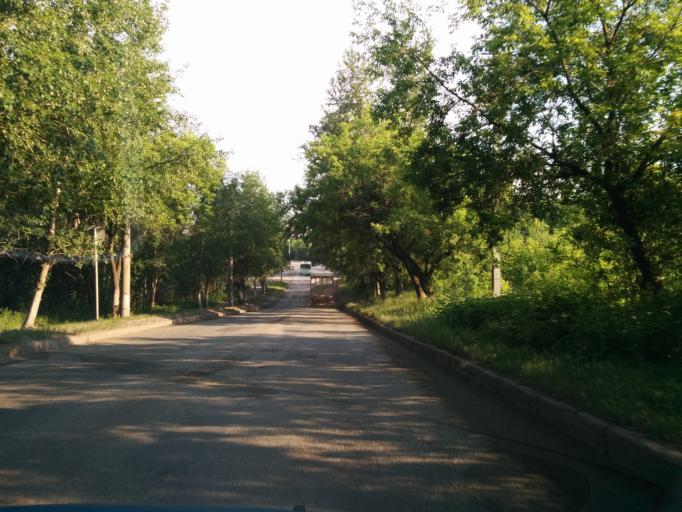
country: RU
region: Perm
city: Perm
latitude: 58.1190
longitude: 56.2929
